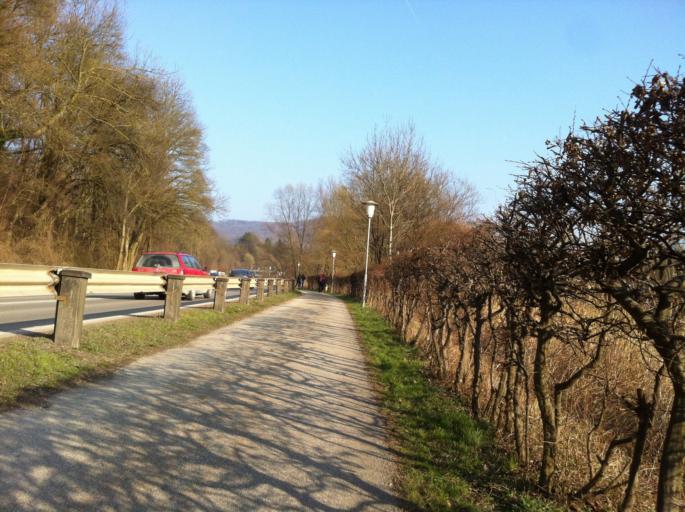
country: AT
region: Lower Austria
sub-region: Politischer Bezirk Wien-Umgebung
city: Pressbaum
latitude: 48.1846
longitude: 16.1085
